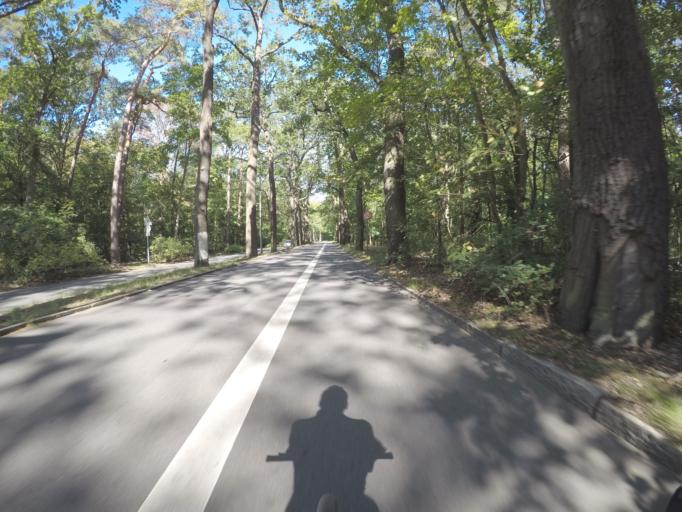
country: DE
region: Berlin
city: Konradshohe
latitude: 52.5775
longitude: 13.2286
